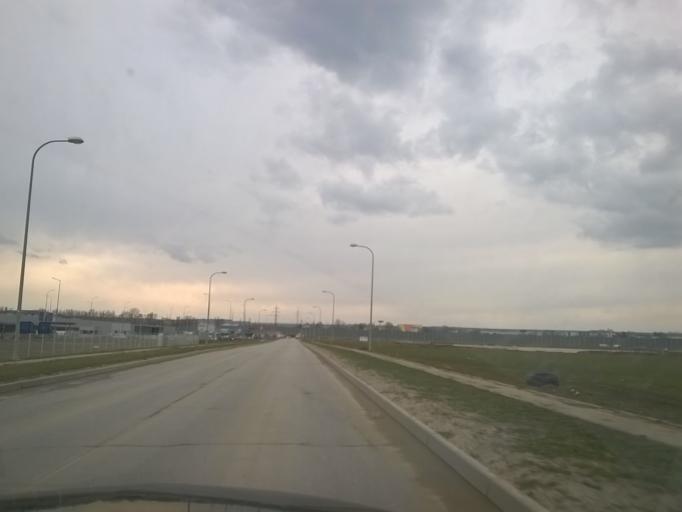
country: SK
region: Nitriansky
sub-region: Okres Nitra
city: Nitra
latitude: 48.3309
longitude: 18.0494
